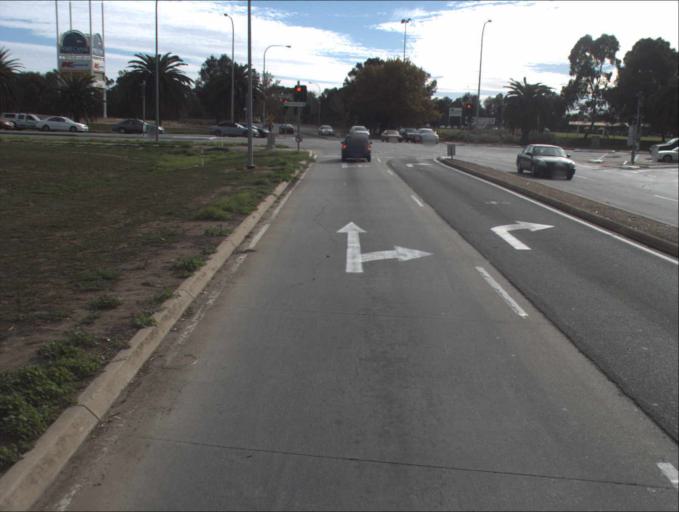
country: AU
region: South Australia
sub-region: Charles Sturt
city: West Lakes Shore
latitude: -34.8531
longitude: 138.5022
